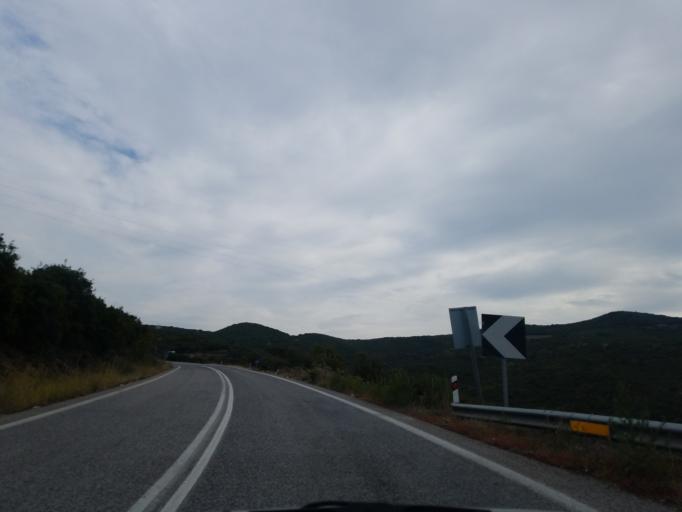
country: GR
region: Central Greece
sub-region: Nomos Fthiotidos
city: Domokos
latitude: 39.1498
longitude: 22.3006
